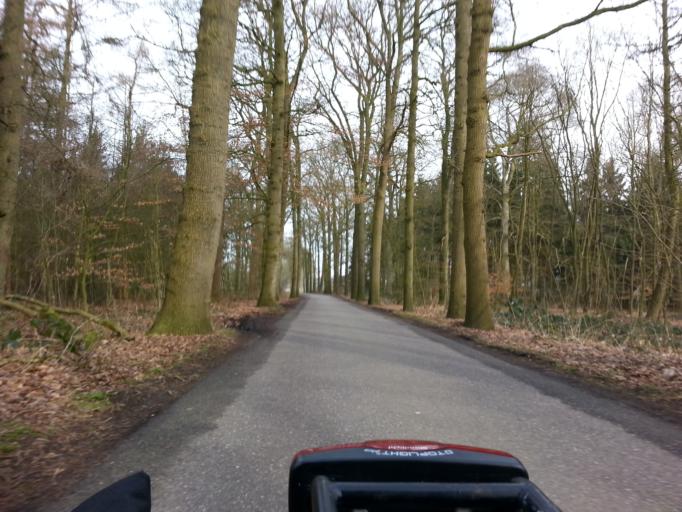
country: NL
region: Utrecht
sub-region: Gemeente Woudenberg
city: Woudenberg
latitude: 52.0887
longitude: 5.3894
